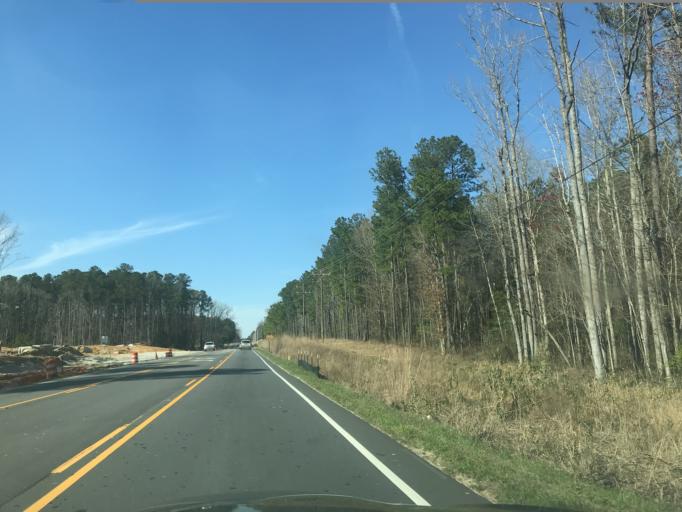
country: US
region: North Carolina
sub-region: Wake County
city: Fuquay-Varina
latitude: 35.5760
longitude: -78.7561
